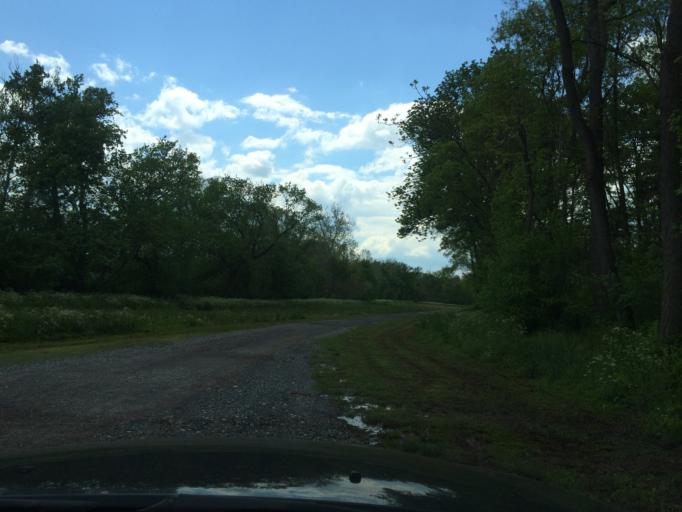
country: US
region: Maryland
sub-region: Carroll County
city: Taneytown
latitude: 39.5835
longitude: -77.2259
